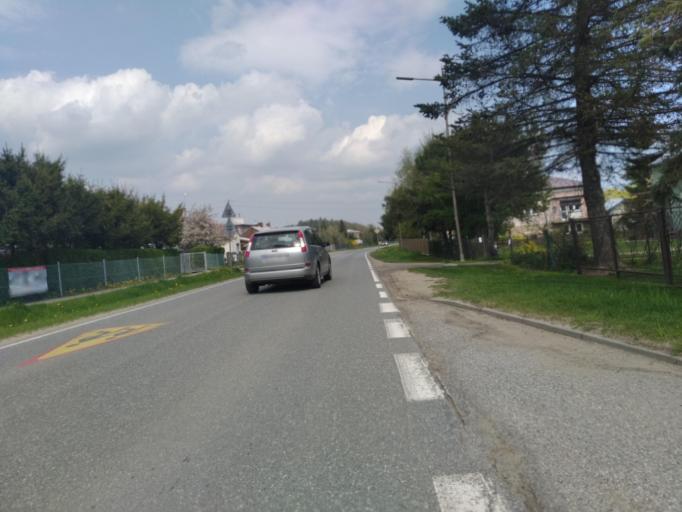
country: PL
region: Subcarpathian Voivodeship
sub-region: Powiat krosnienski
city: Rymanow
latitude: 49.5633
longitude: 21.8601
